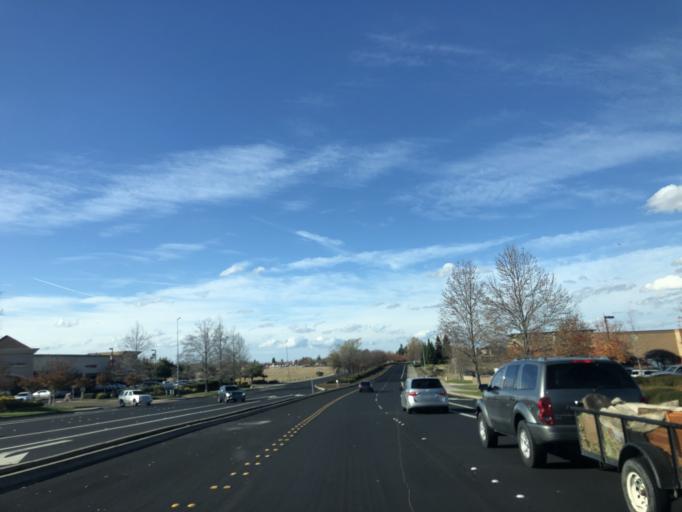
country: US
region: California
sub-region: Placer County
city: Roseville
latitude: 38.7785
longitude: -121.2882
